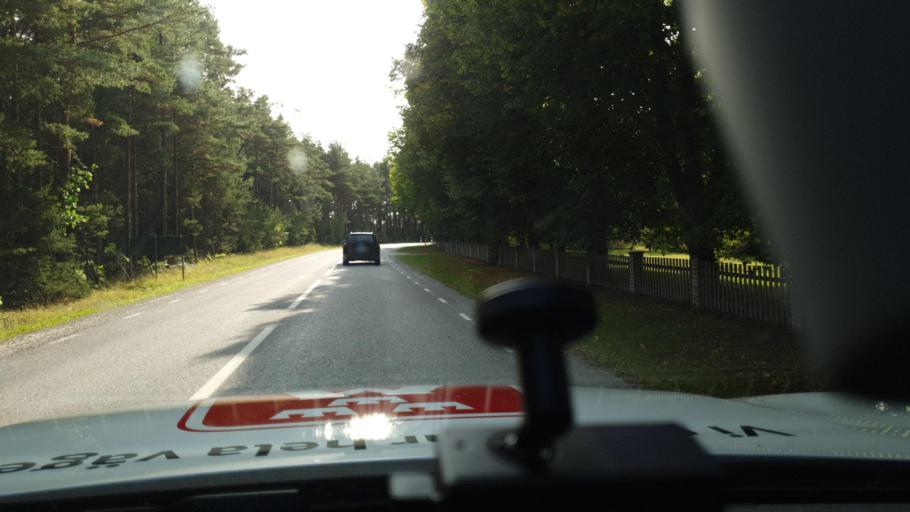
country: SE
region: Gotland
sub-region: Gotland
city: Visby
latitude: 57.6729
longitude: 18.4834
